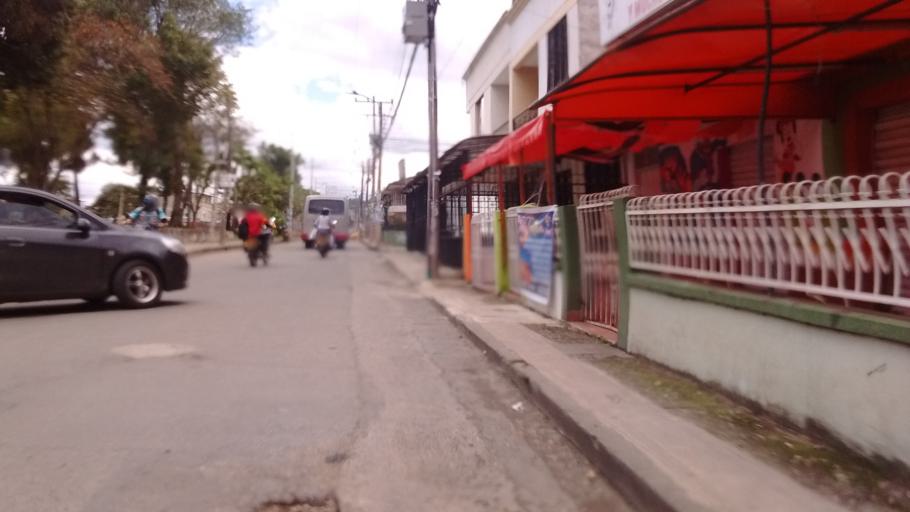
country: CO
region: Cauca
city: Popayan
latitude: 2.4579
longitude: -76.5876
